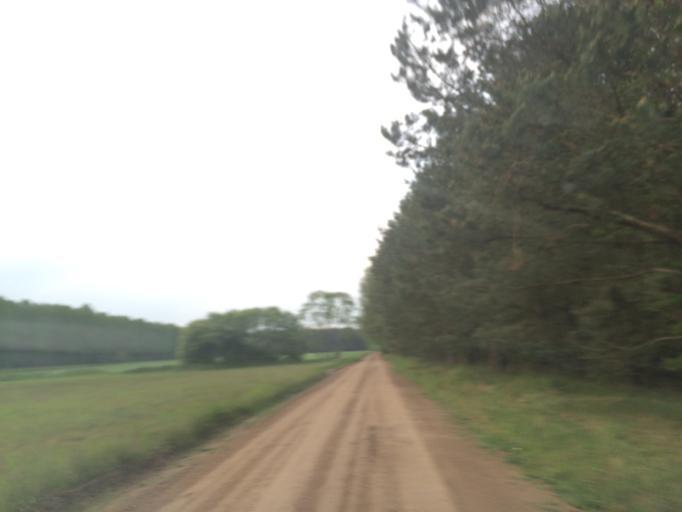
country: PL
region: Warmian-Masurian Voivodeship
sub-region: Powiat nowomiejski
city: Kurzetnik
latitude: 53.3505
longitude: 19.5145
